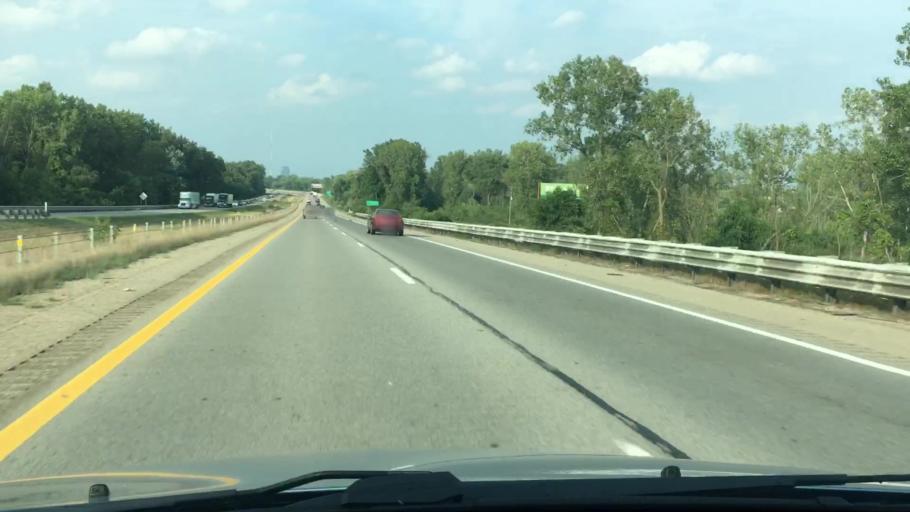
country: US
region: Michigan
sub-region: Kent County
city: Wyoming
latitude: 42.9354
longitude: -85.7208
